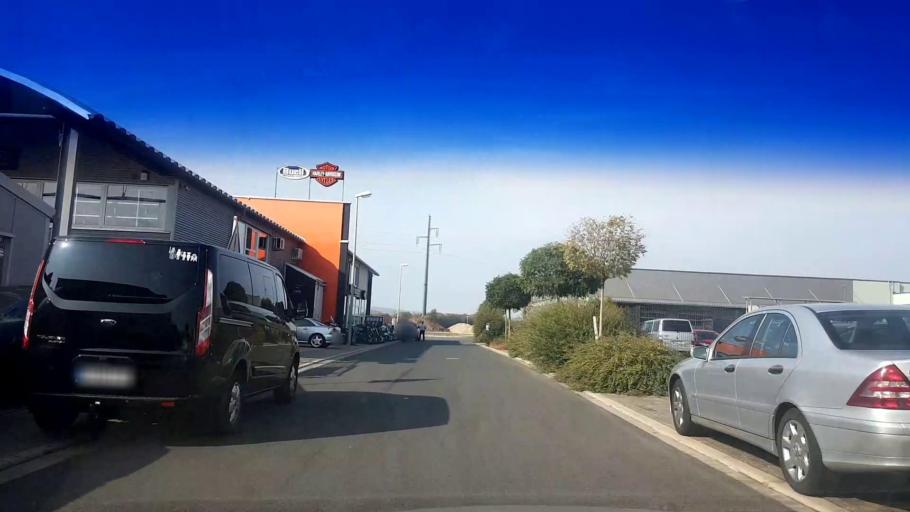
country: DE
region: Bavaria
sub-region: Upper Franconia
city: Viereth-Trunstadt
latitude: 49.9366
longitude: 10.7803
